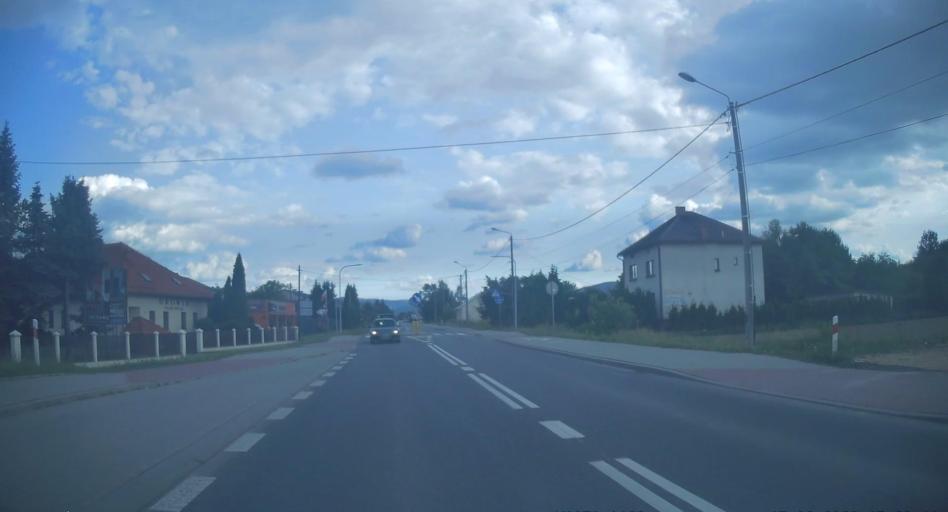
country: PL
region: Lesser Poland Voivodeship
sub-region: Powiat oswiecimski
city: Nowa Wies
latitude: 49.8968
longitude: 19.2183
